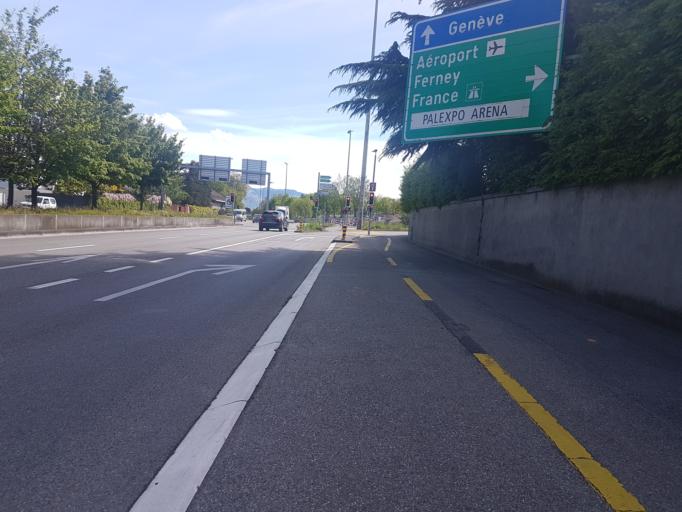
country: CH
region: Geneva
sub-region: Geneva
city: Bellevue
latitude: 46.2500
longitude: 6.1507
